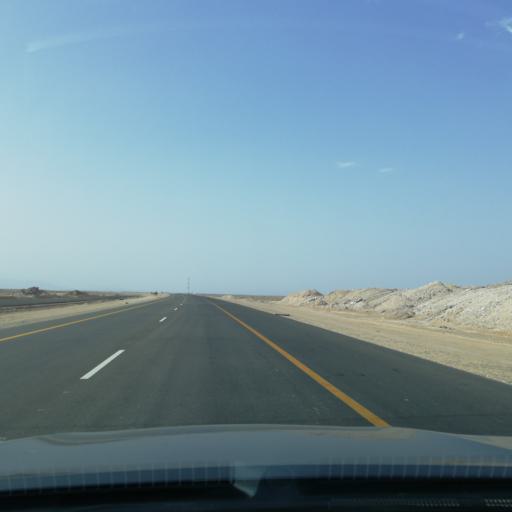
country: OM
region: Muhafazat ad Dakhiliyah
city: Adam
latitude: 22.1290
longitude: 57.5257
